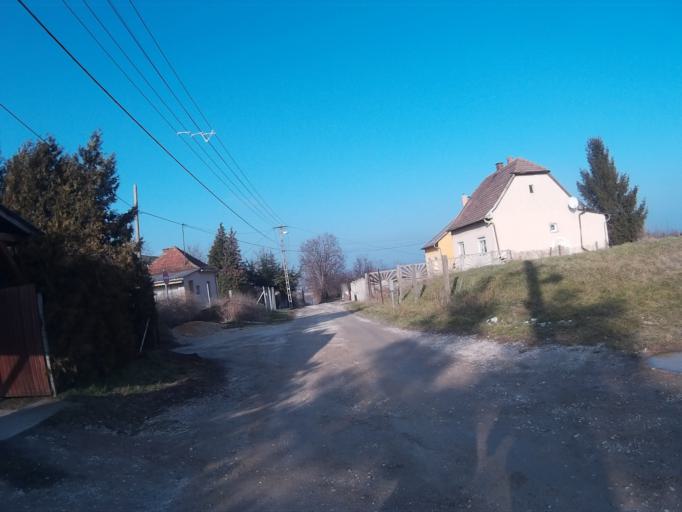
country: HU
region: Komarom-Esztergom
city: Labatlan
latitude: 47.7461
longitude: 18.4845
